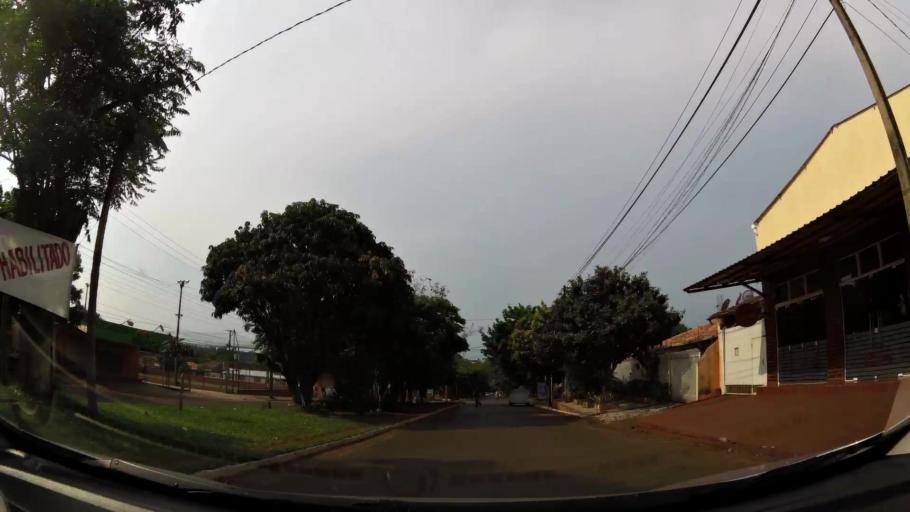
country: PY
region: Alto Parana
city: Ciudad del Este
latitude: -25.4969
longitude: -54.6505
